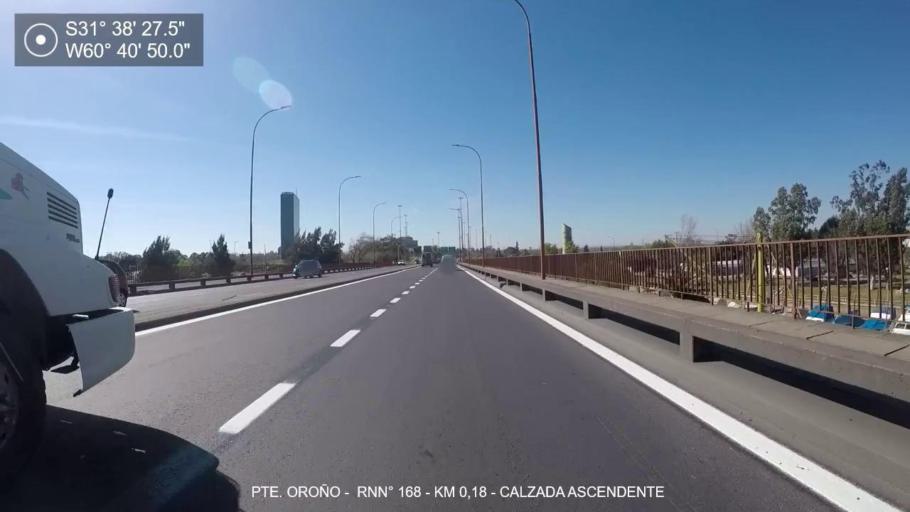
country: AR
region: Santa Fe
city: Santa Fe de la Vera Cruz
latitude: -31.6413
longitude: -60.6810
